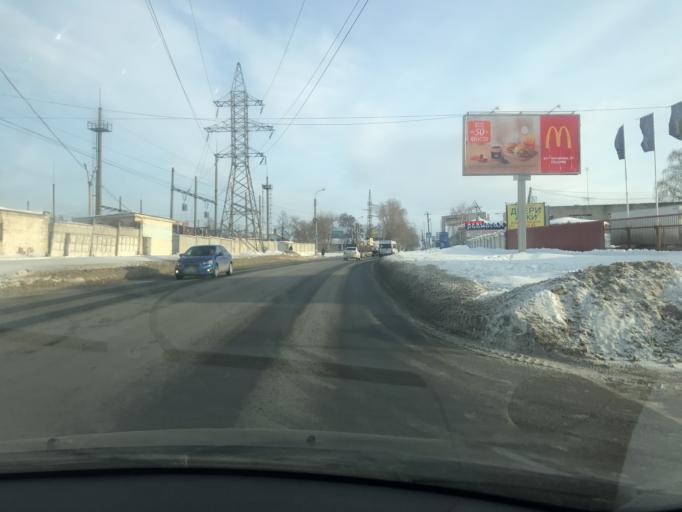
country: RU
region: Ulyanovsk
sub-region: Ulyanovskiy Rayon
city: Ulyanovsk
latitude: 54.3313
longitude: 48.3645
